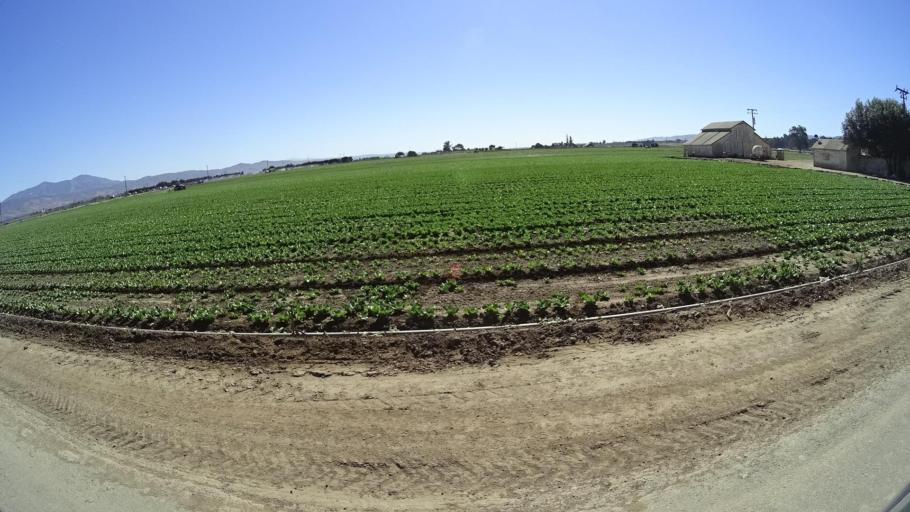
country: US
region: California
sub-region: Monterey County
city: Soledad
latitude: 36.3917
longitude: -121.3476
